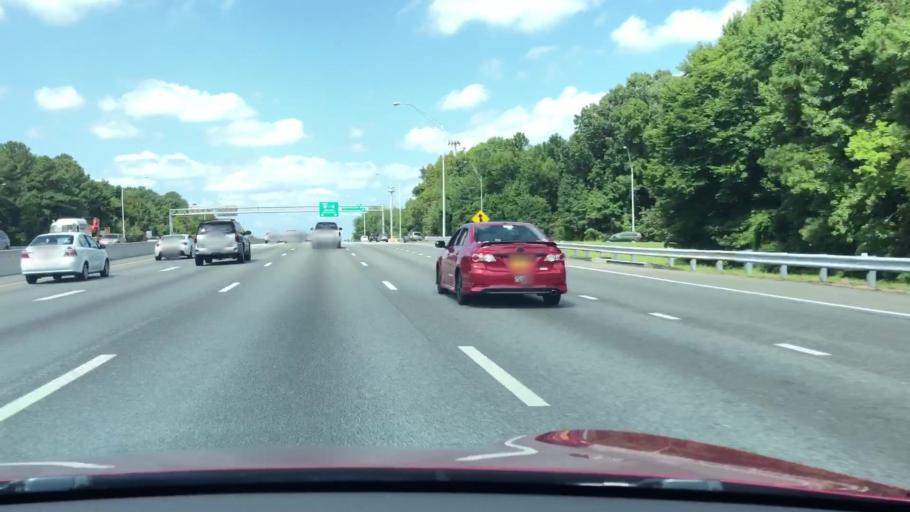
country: US
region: Virginia
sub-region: City of Chesapeake
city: Chesapeake
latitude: 36.8344
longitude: -76.1342
